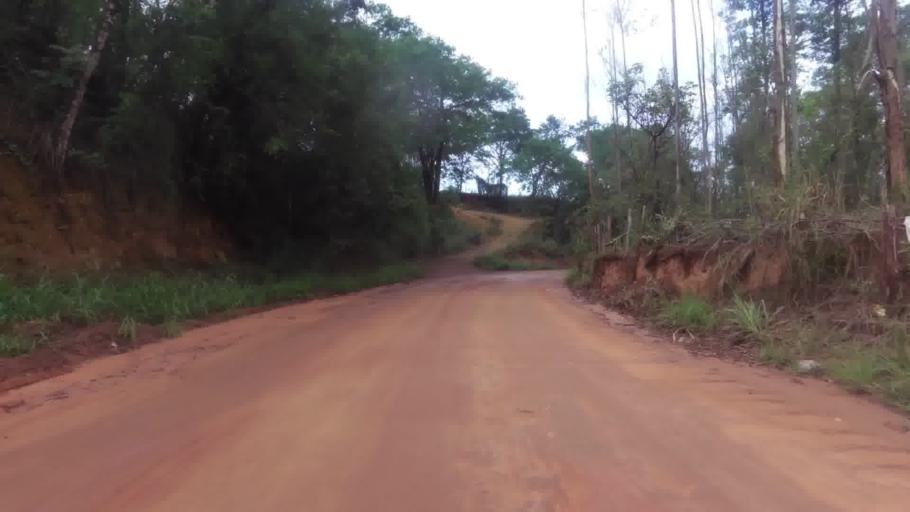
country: BR
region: Espirito Santo
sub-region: Piuma
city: Piuma
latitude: -20.7828
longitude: -40.6306
